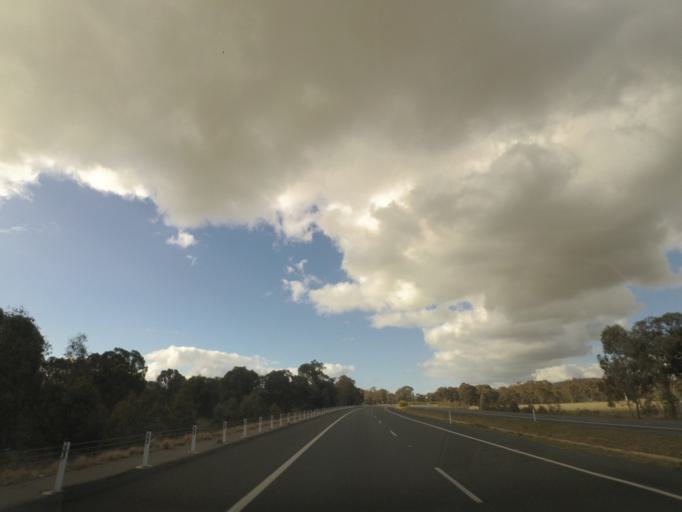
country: AU
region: New South Wales
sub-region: Greater Hume Shire
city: Holbrook
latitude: -35.7077
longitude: 147.3090
